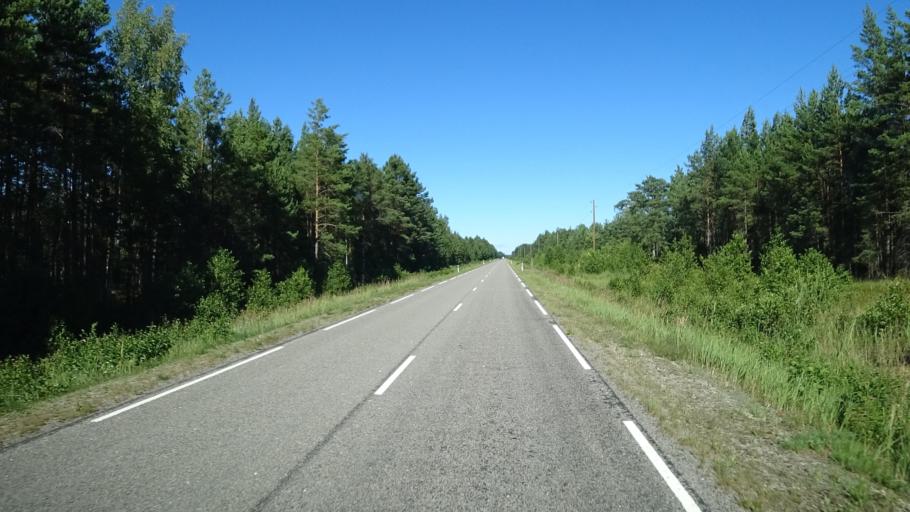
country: LV
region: Dundaga
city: Dundaga
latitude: 57.7012
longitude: 22.4215
